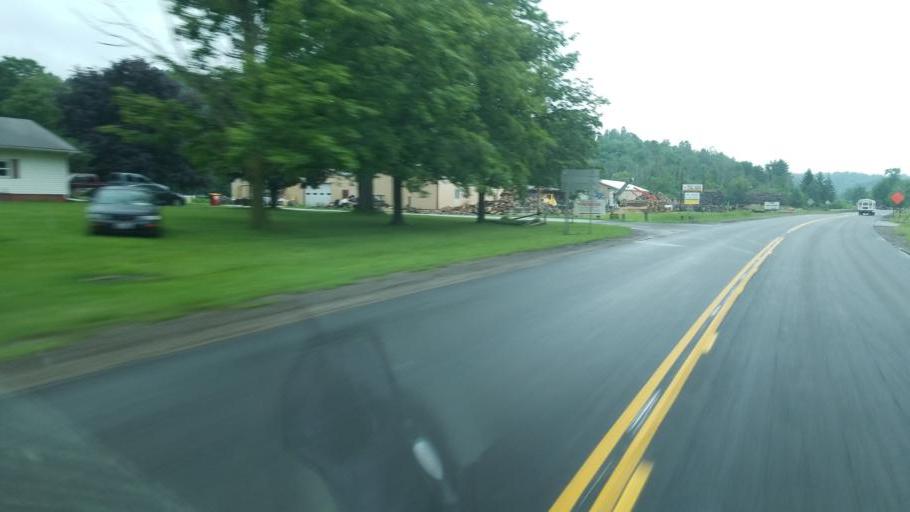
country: US
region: Ohio
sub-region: Tuscarawas County
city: Dennison
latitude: 40.3893
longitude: -81.2613
